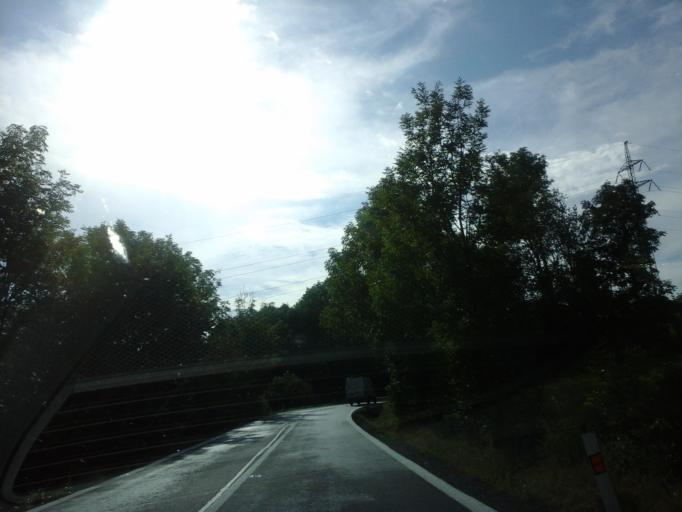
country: CZ
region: Olomoucky
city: Stity
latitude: 49.9625
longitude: 16.7327
